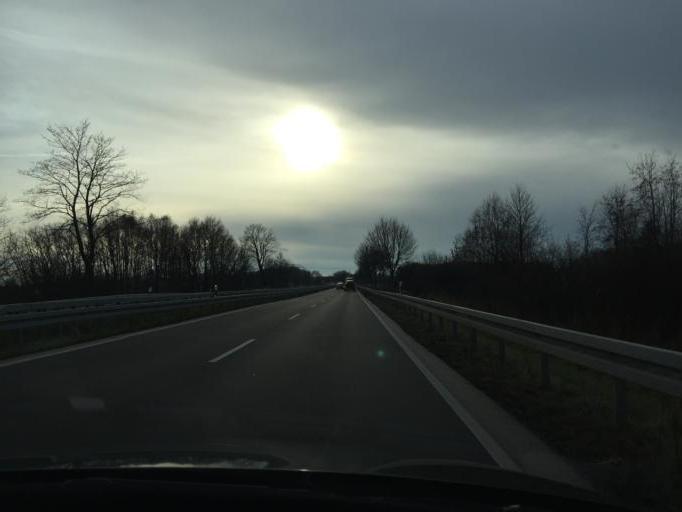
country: DE
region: Brandenburg
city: Peitz
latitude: 51.8252
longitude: 14.3865
